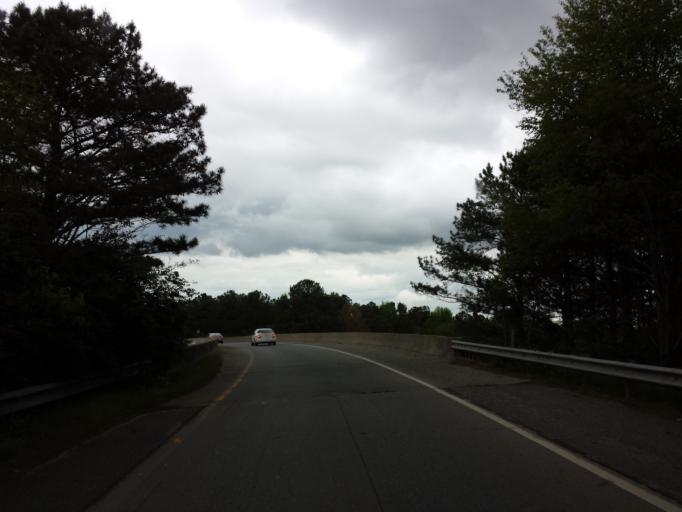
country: US
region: Georgia
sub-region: Cobb County
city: Marietta
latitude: 33.9855
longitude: -84.5399
